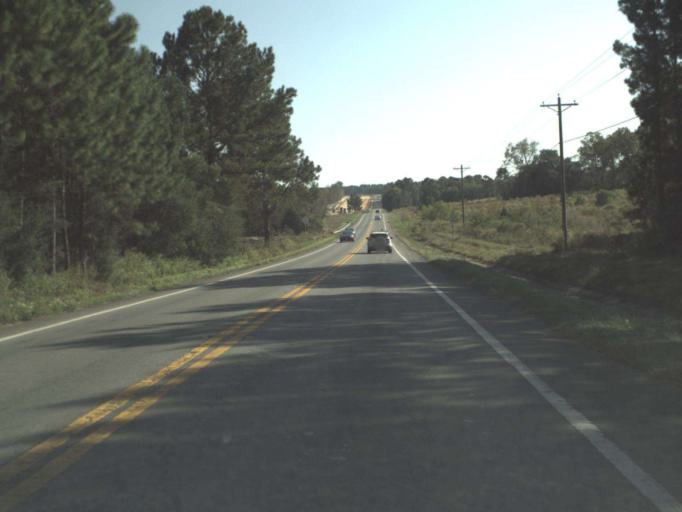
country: US
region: Florida
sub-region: Walton County
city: DeFuniak Springs
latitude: 30.6855
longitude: -86.1227
